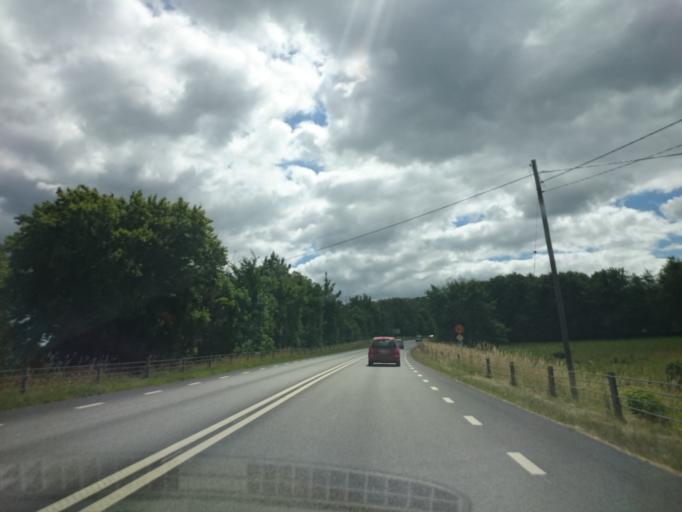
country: SE
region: Skane
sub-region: Kristianstads Kommun
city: Degeberga
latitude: 55.8039
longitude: 14.1475
